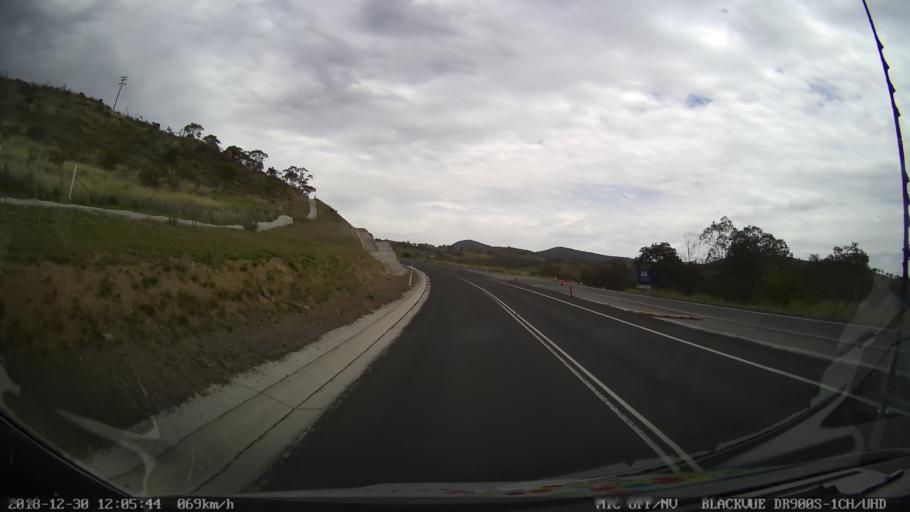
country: AU
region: New South Wales
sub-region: Snowy River
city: Jindabyne
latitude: -36.4124
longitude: 148.6020
